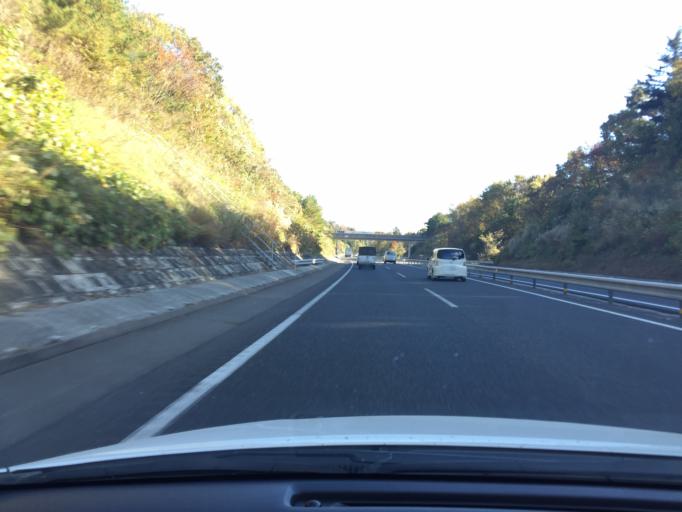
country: JP
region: Fukushima
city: Funehikimachi-funehiki
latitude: 37.3377
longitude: 140.6117
